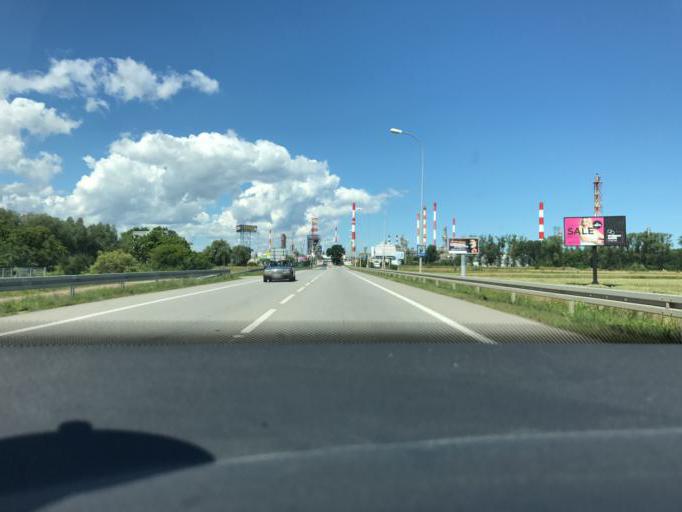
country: PL
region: Pomeranian Voivodeship
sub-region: Gdansk
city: Gdansk
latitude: 54.3356
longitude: 18.7411
